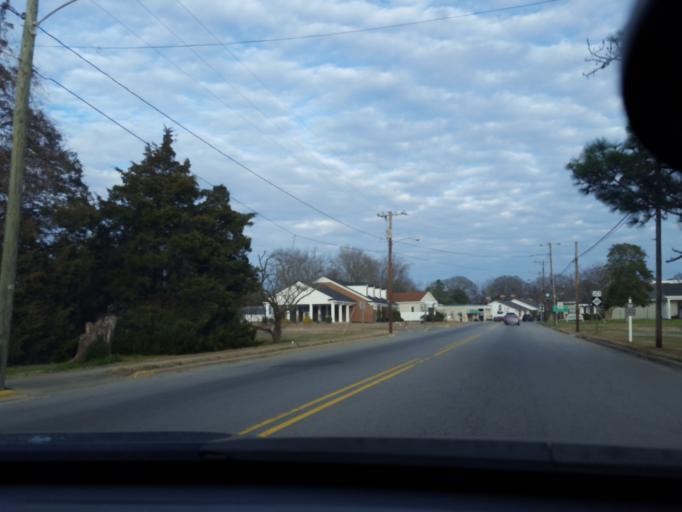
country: US
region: North Carolina
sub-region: Northampton County
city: Jackson
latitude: 36.3891
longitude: -77.4234
